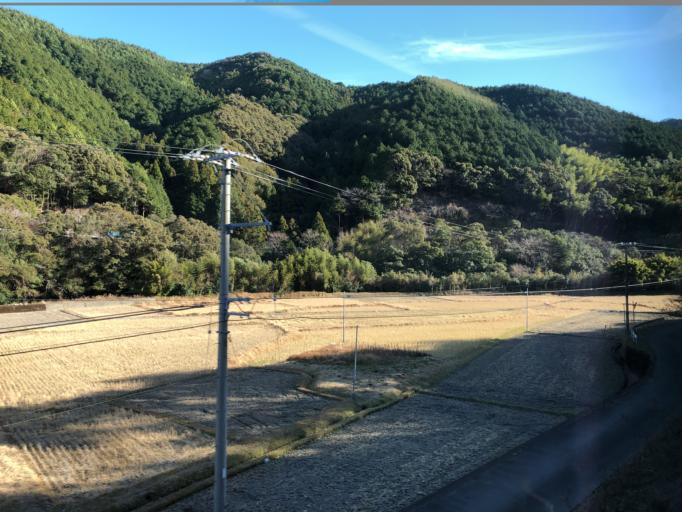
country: JP
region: Kochi
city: Nakamura
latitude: 33.1137
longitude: 133.1115
